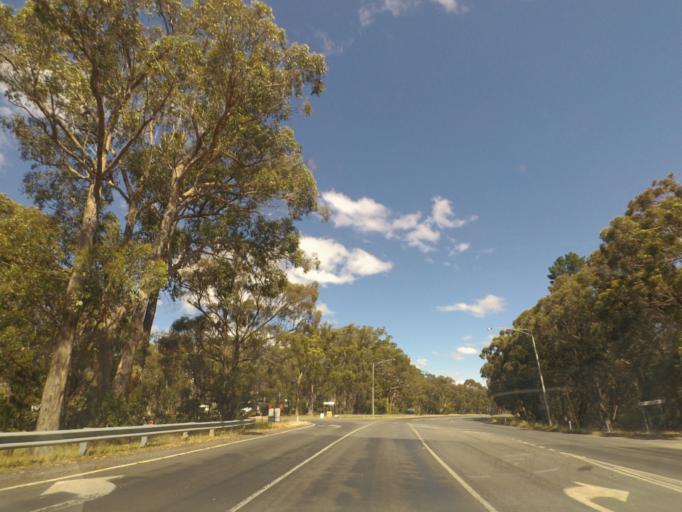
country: AU
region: Victoria
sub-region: Hume
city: Sunbury
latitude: -37.4182
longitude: 144.5513
